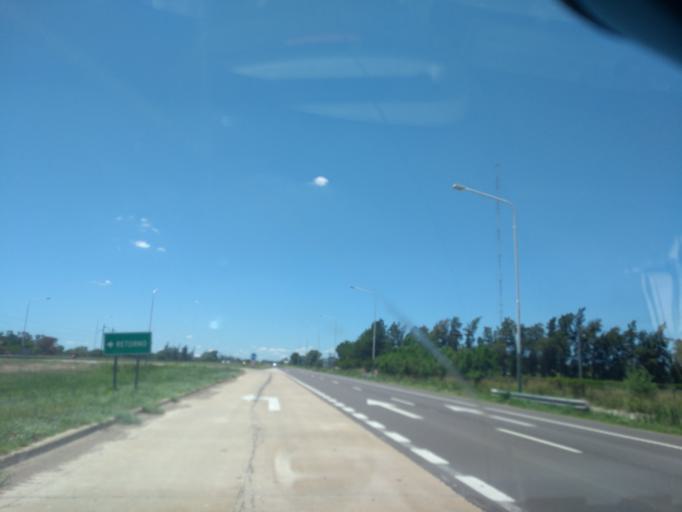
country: AR
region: Chaco
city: Puerto Tirol
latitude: -27.3764
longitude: -59.0451
